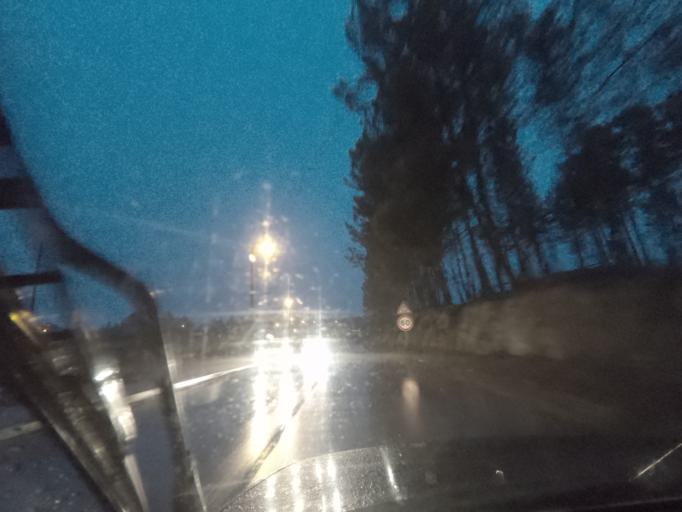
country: PT
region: Vila Real
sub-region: Vila Real
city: Vila Real
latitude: 41.2833
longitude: -7.7044
